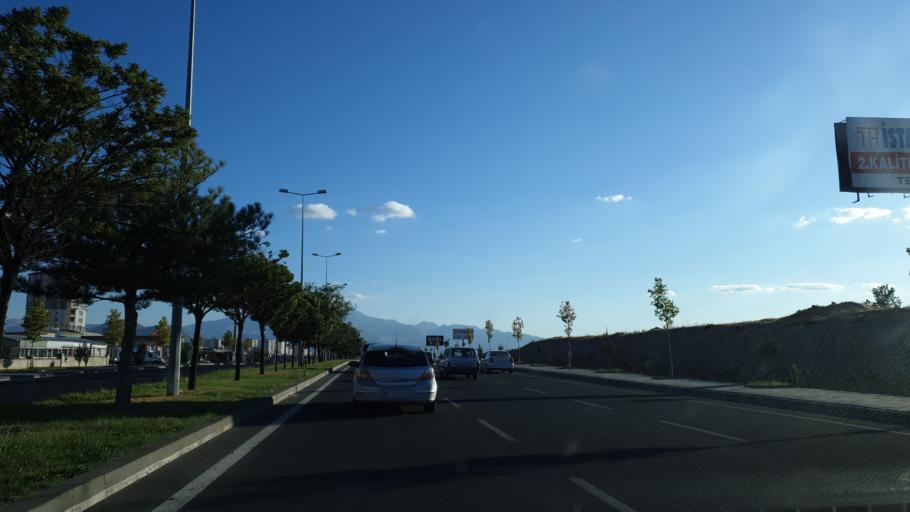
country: TR
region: Kayseri
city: Kocasinan
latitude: 38.7794
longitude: 35.5755
